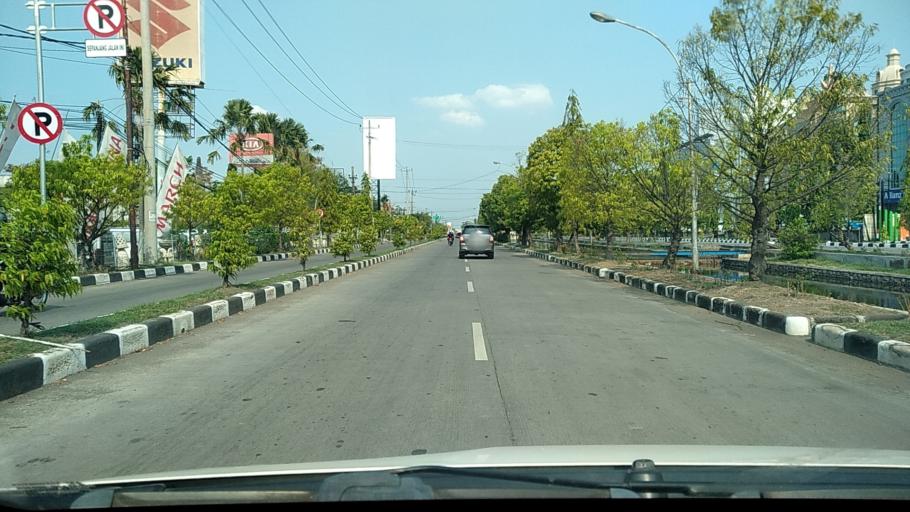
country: ID
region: Central Java
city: Semarang
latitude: -6.9623
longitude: 110.3913
